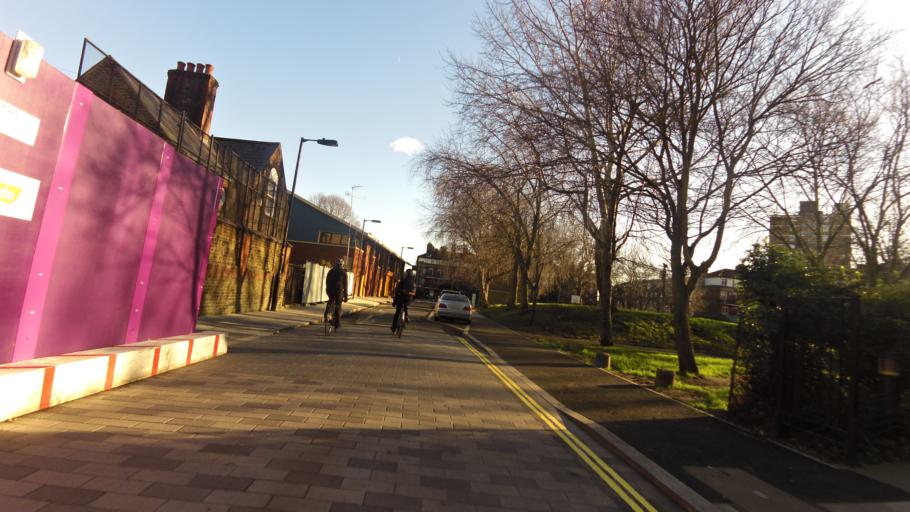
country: GB
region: England
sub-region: Greater London
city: City of London
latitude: 51.4956
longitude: -0.0824
